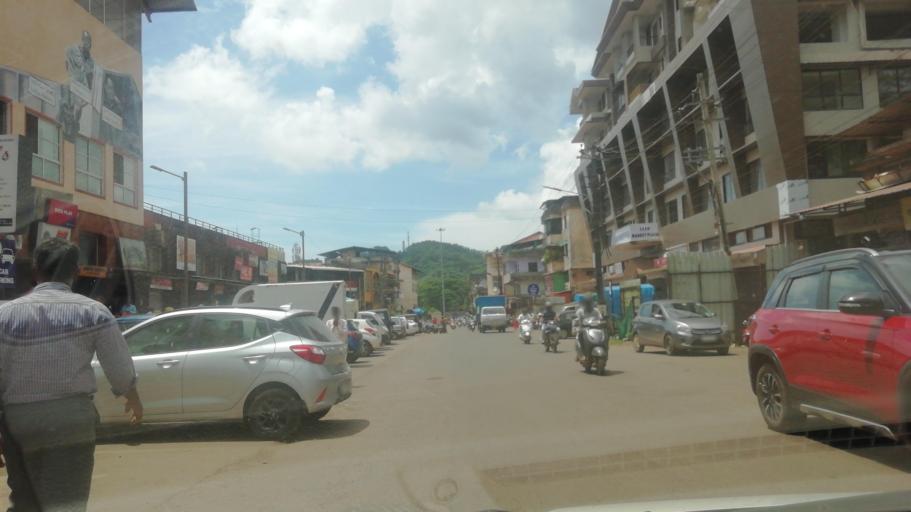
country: IN
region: Goa
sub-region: North Goa
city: Ponda
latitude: 15.4025
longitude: 74.0097
